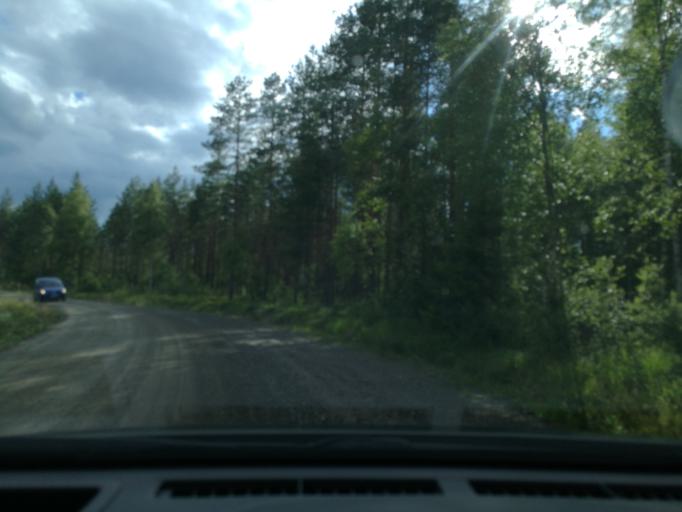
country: SE
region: Vaestmanland
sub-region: Surahammars Kommun
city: Ramnas
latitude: 59.8126
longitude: 16.2358
